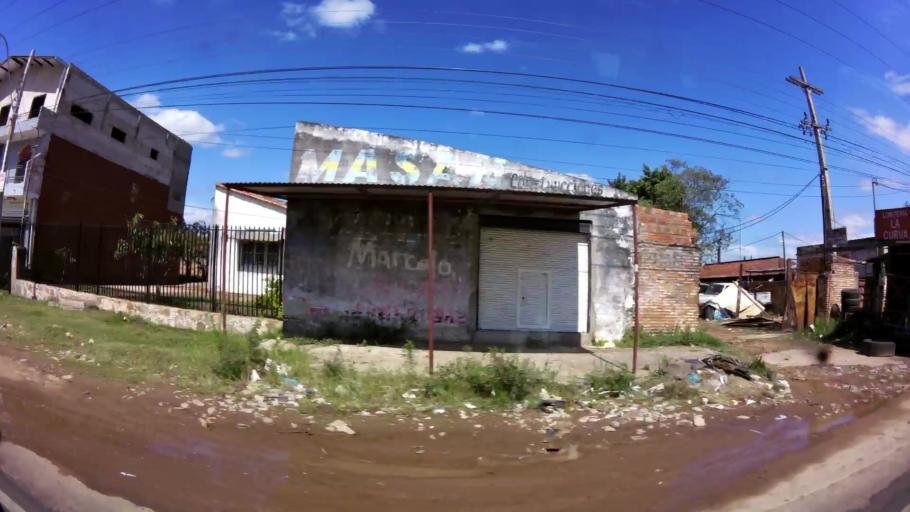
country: PY
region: Central
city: Fernando de la Mora
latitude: -25.2774
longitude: -57.5235
